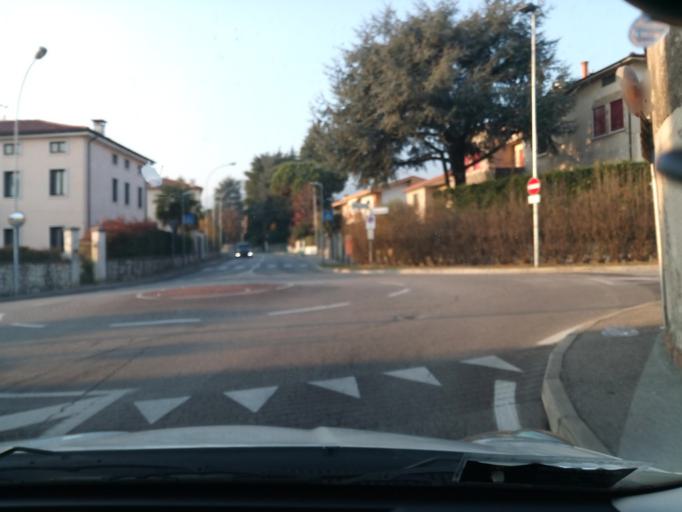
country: IT
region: Veneto
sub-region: Provincia di Vicenza
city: Schio
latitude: 45.7144
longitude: 11.3739
